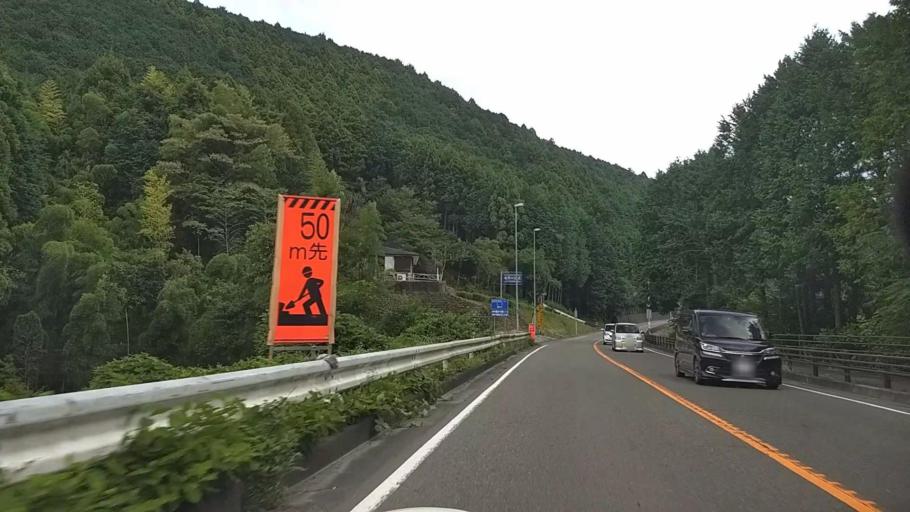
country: JP
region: Shizuoka
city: Fujinomiya
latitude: 35.2235
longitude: 138.5193
